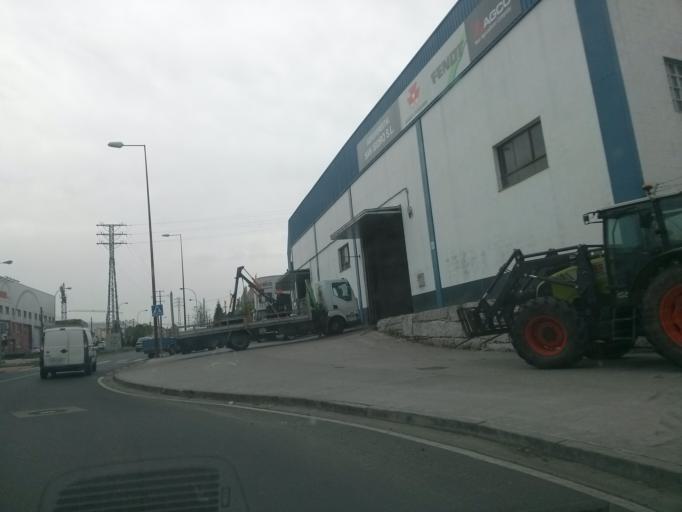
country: ES
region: Galicia
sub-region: Provincia de Lugo
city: Lugo
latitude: 43.0440
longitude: -7.5614
